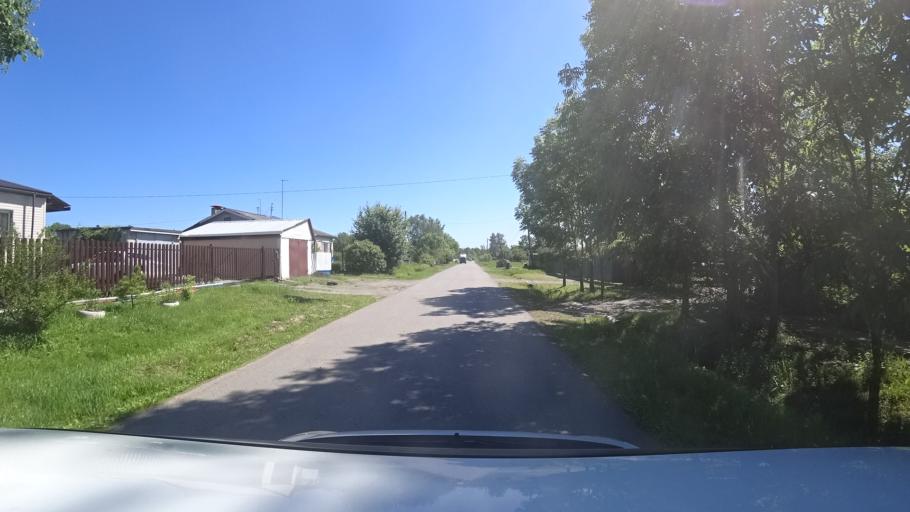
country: RU
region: Khabarovsk Krai
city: Topolevo
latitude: 48.5580
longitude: 135.1904
